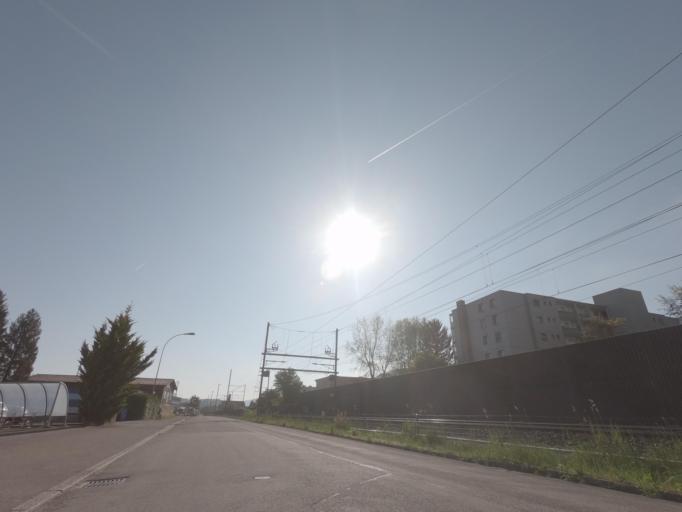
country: CH
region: Bern
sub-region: Biel/Bienne District
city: Lengnau
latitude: 47.1853
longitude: 7.3807
